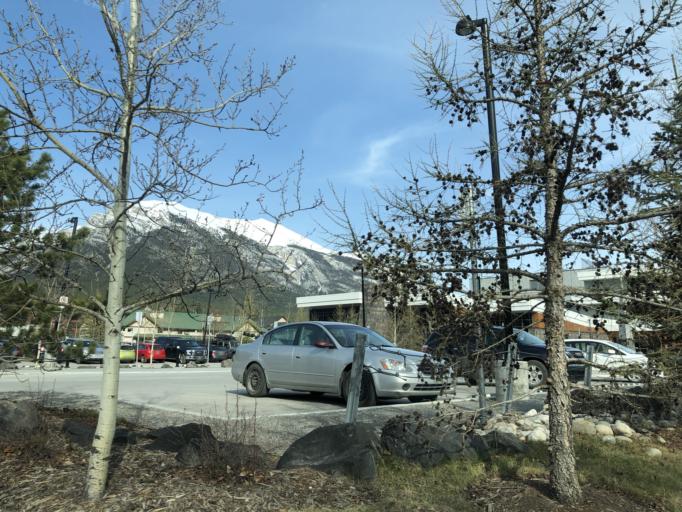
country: CA
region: Alberta
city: Canmore
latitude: 51.0894
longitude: -115.3521
